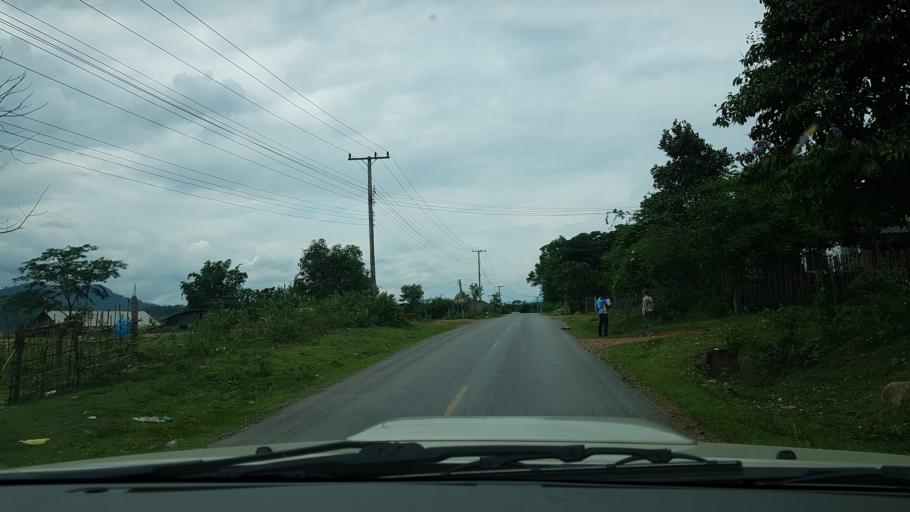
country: LA
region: Loungnamtha
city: Muang Nale
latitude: 20.3501
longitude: 101.6831
